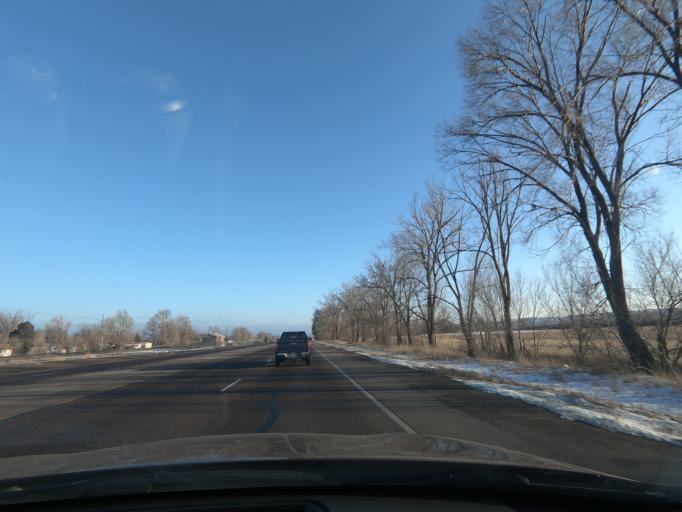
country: US
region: Colorado
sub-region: El Paso County
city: Stratmoor
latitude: 38.7582
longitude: -104.7508
